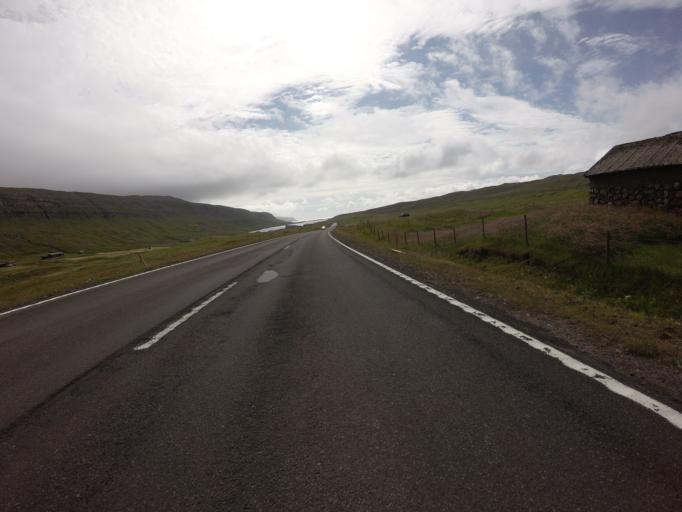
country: FO
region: Sandoy
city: Sandur
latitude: 61.8646
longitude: -6.8387
